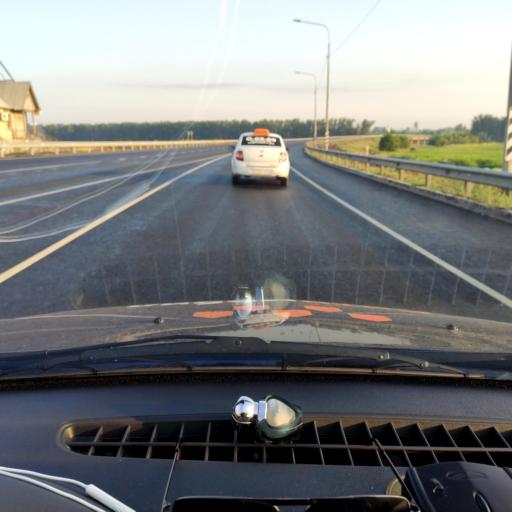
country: RU
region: Lipetsk
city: Yelets
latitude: 52.5810
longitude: 38.5127
